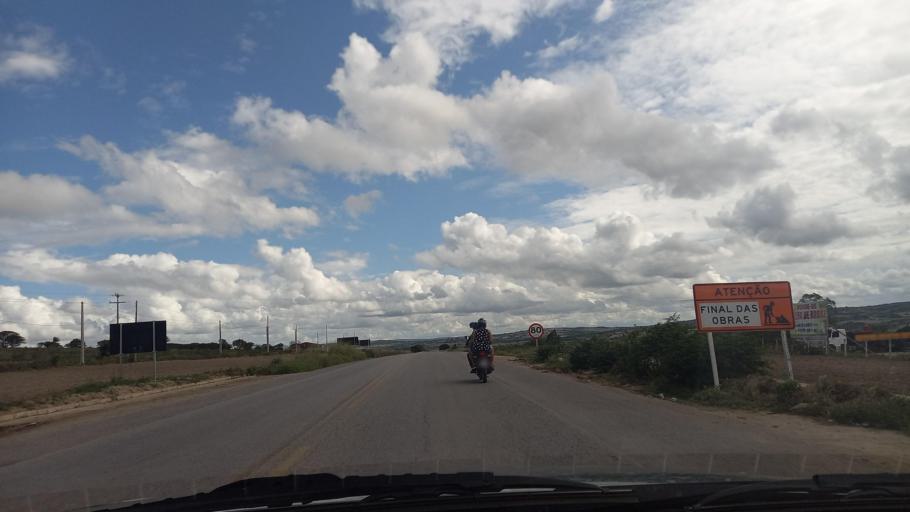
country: BR
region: Pernambuco
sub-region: Lajedo
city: Lajedo
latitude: -8.7209
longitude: -36.4258
